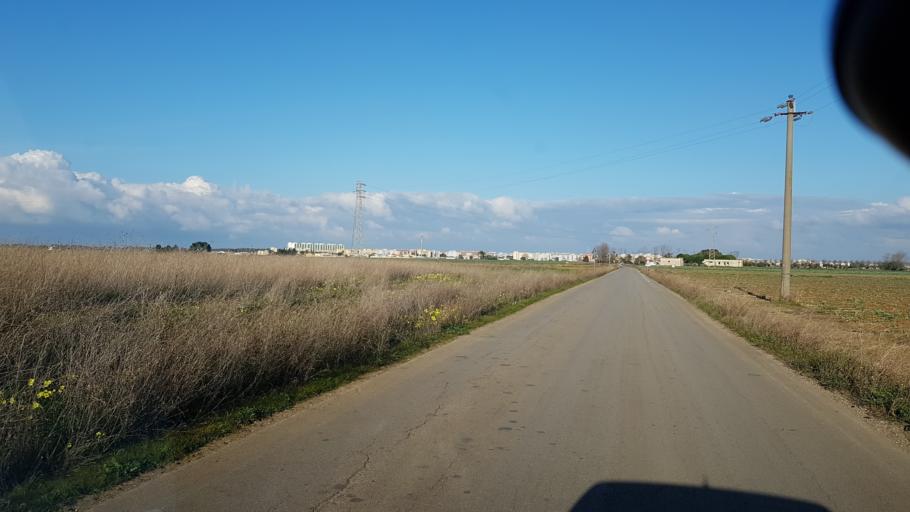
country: IT
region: Apulia
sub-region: Provincia di Brindisi
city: Brindisi
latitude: 40.6042
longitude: 17.9080
